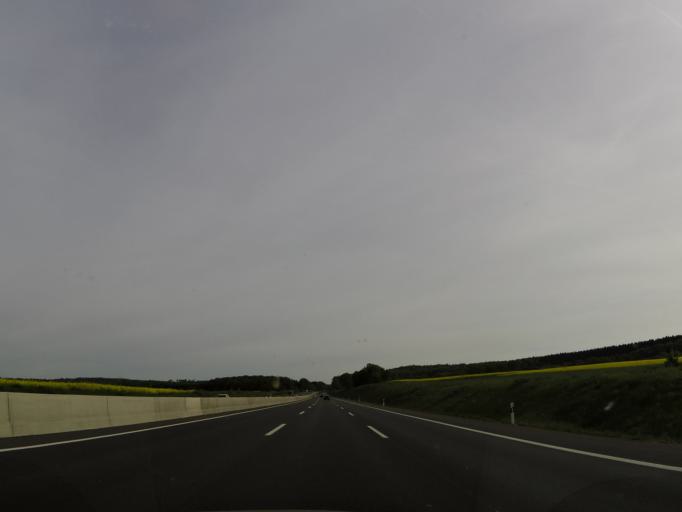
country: DE
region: Lower Saxony
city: Bockenem
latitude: 52.0245
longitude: 10.1705
